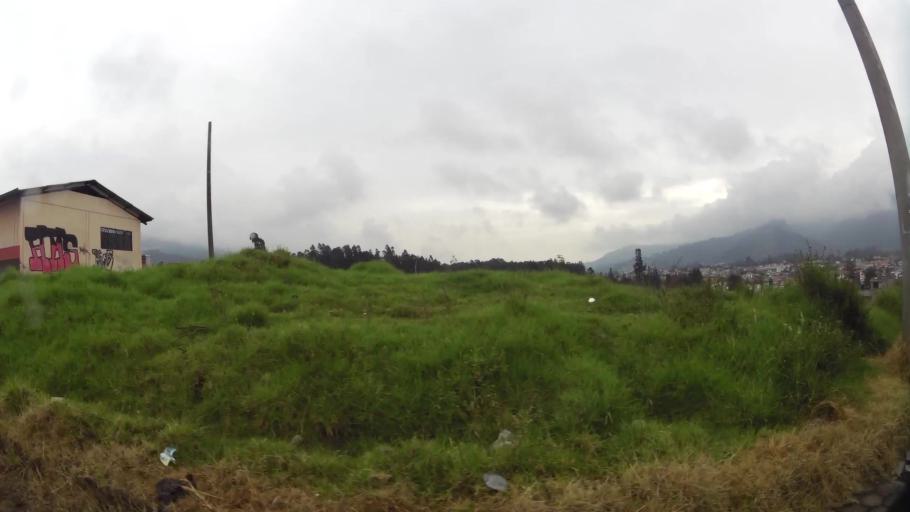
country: EC
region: Pichincha
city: Sangolqui
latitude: -0.2754
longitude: -78.4714
